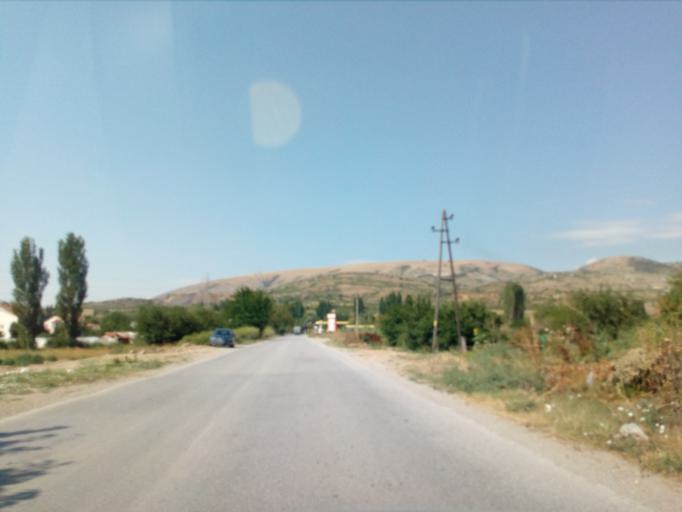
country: MK
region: Veles
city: Veles
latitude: 41.7444
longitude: 21.7642
